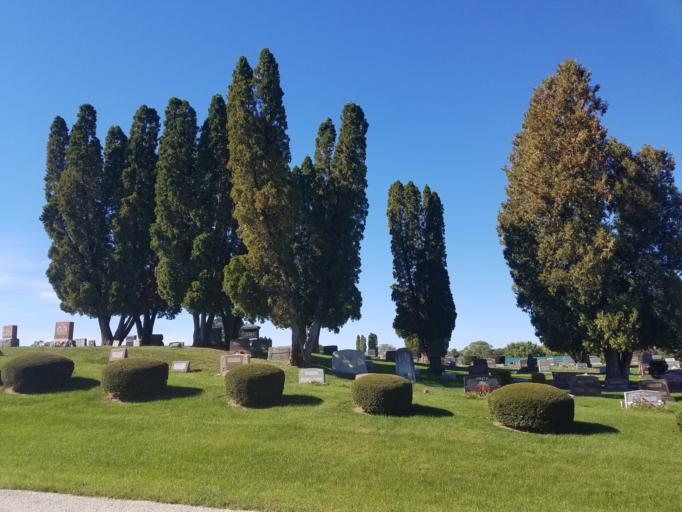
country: US
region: Ohio
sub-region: Richland County
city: Lexington
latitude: 40.6307
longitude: -82.6487
